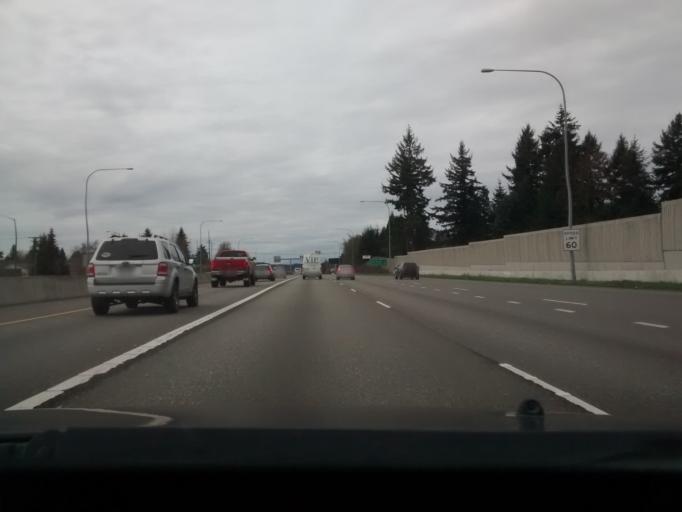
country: US
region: Washington
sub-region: Pierce County
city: Fircrest
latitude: 47.2583
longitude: -122.5215
